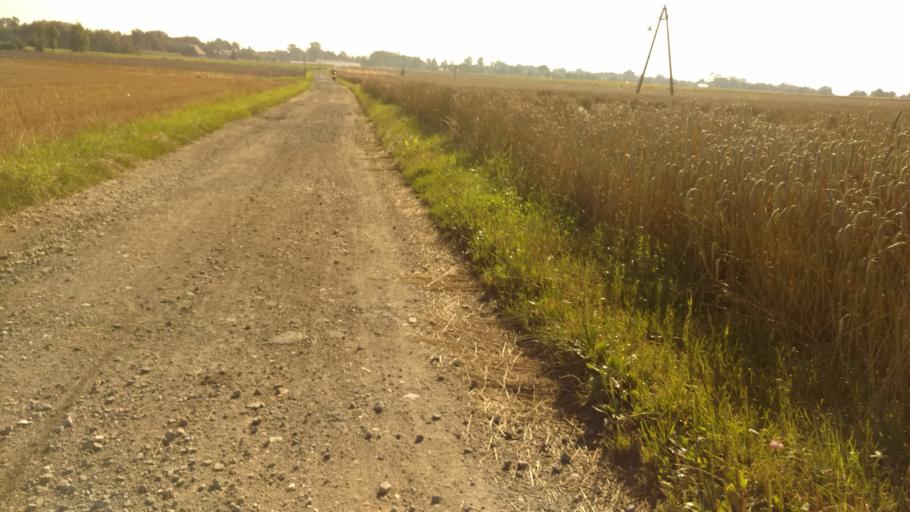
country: PL
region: Silesian Voivodeship
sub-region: Powiat pszczynski
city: Pszczyna
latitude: 49.9792
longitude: 18.9706
